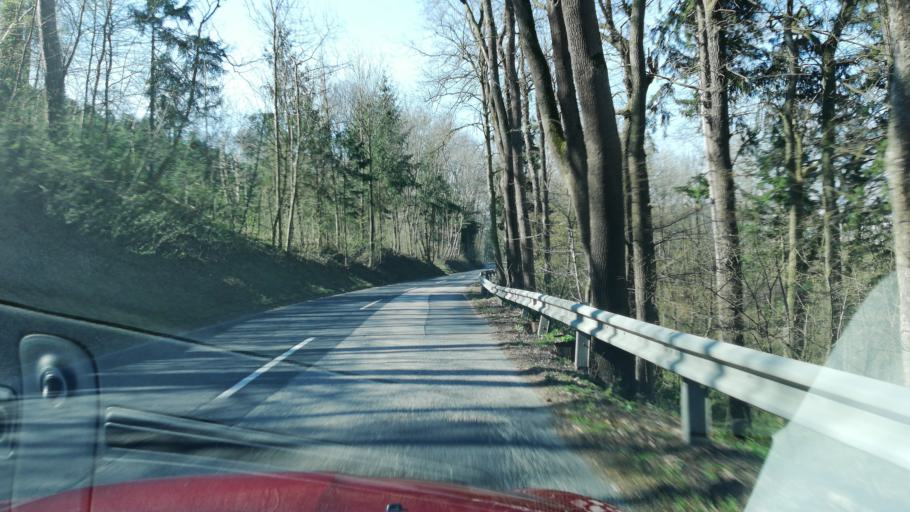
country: AT
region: Upper Austria
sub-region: Wels-Land
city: Thalheim bei Wels
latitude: 48.1547
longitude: 14.0529
